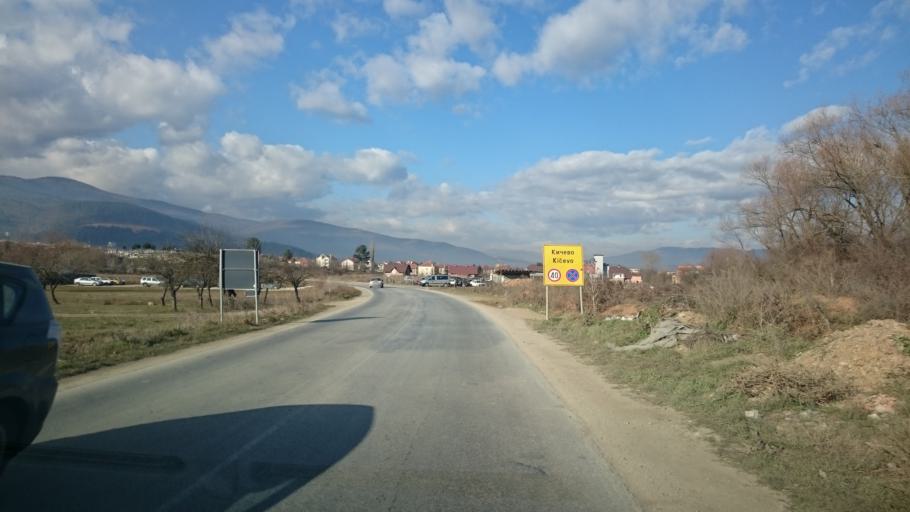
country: MK
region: Kicevo
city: Kicevo
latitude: 41.4973
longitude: 20.9623
